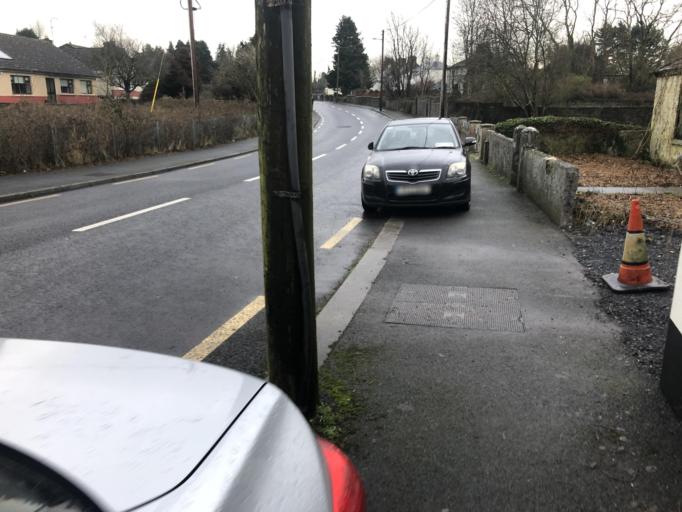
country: IE
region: Connaught
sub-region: County Galway
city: Tuam
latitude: 53.5186
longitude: -8.8403
